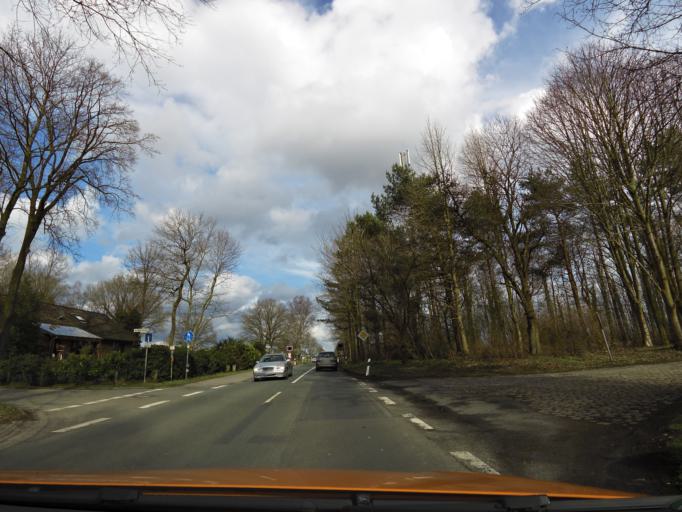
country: DE
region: Lower Saxony
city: Dotlingen
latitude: 52.9383
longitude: 8.4253
